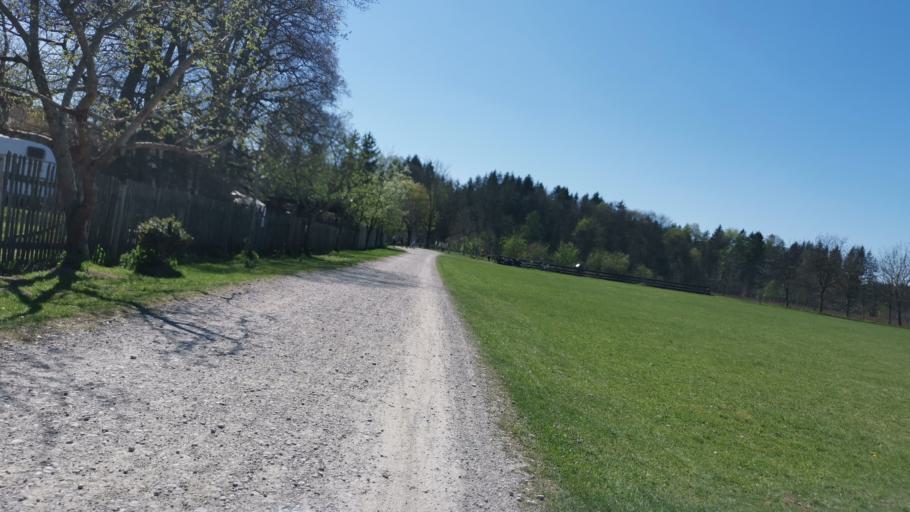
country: DE
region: Bavaria
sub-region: Upper Bavaria
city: Planegg
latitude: 48.0763
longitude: 11.4178
